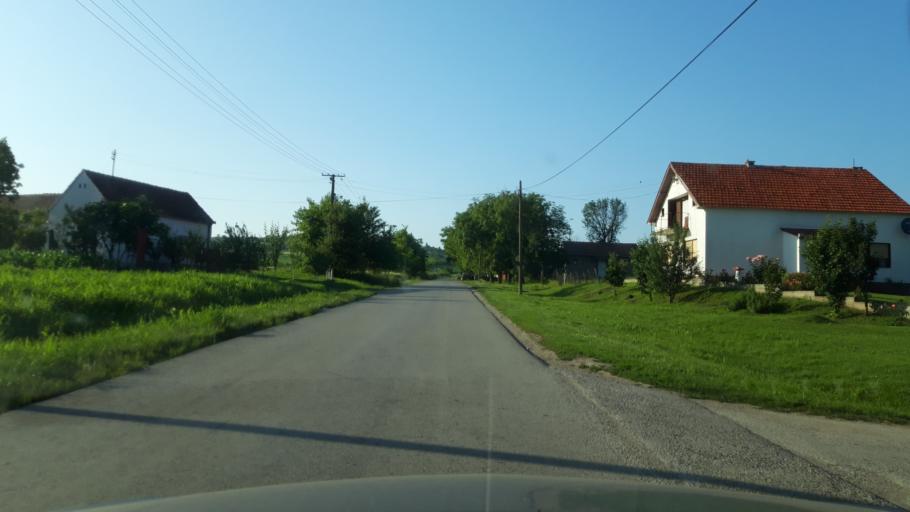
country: RS
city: Celarevo
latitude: 45.1173
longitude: 19.5093
